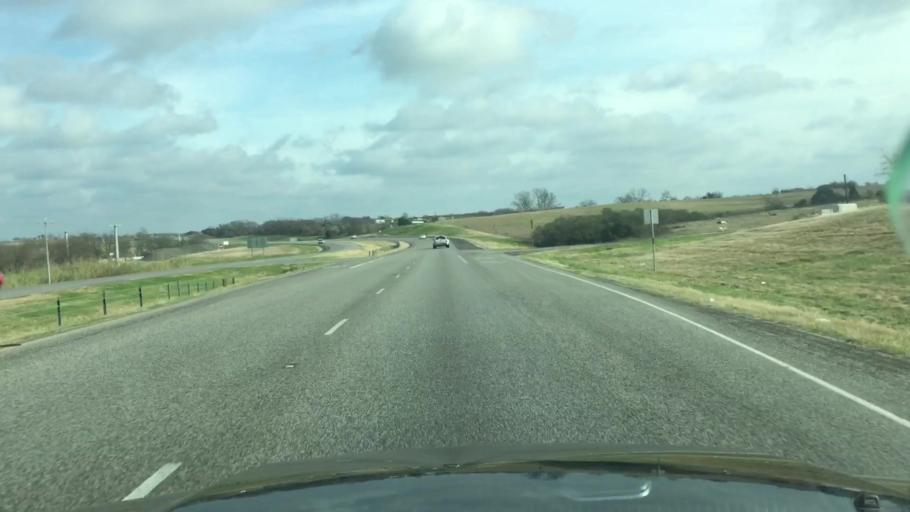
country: US
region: Texas
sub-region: Washington County
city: Brenham
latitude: 30.1385
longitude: -96.3526
